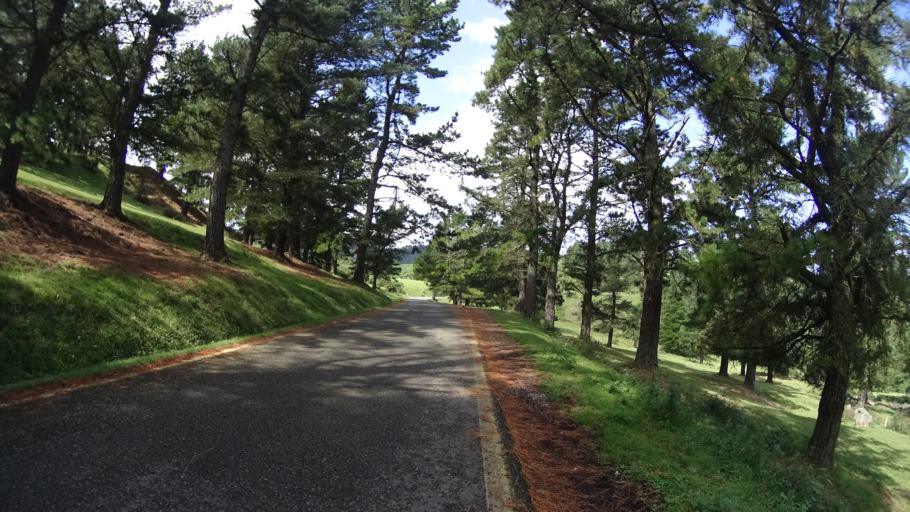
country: ES
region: Basque Country
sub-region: Bizkaia
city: Urtuella
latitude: 43.2833
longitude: -3.0635
